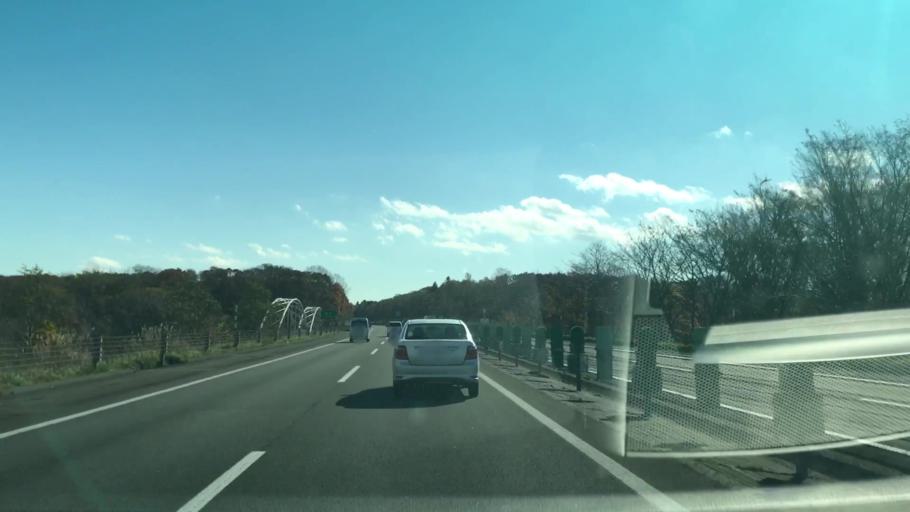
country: JP
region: Hokkaido
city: Chitose
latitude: 42.8638
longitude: 141.5579
